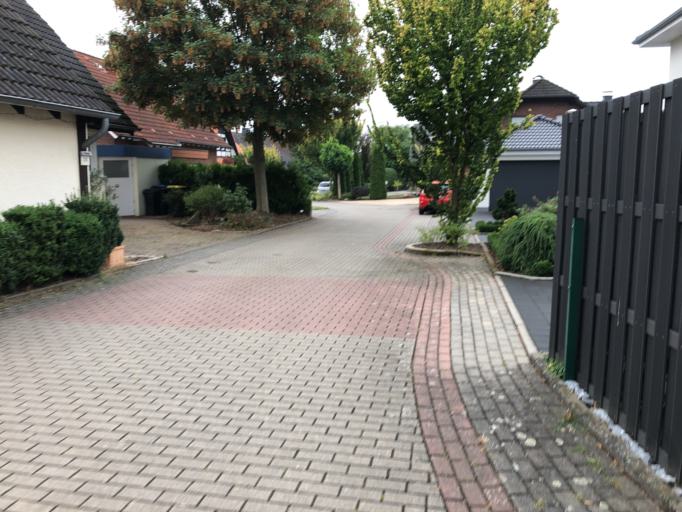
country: DE
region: North Rhine-Westphalia
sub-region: Regierungsbezirk Arnsberg
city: Frondenberg
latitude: 51.4766
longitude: 7.7286
